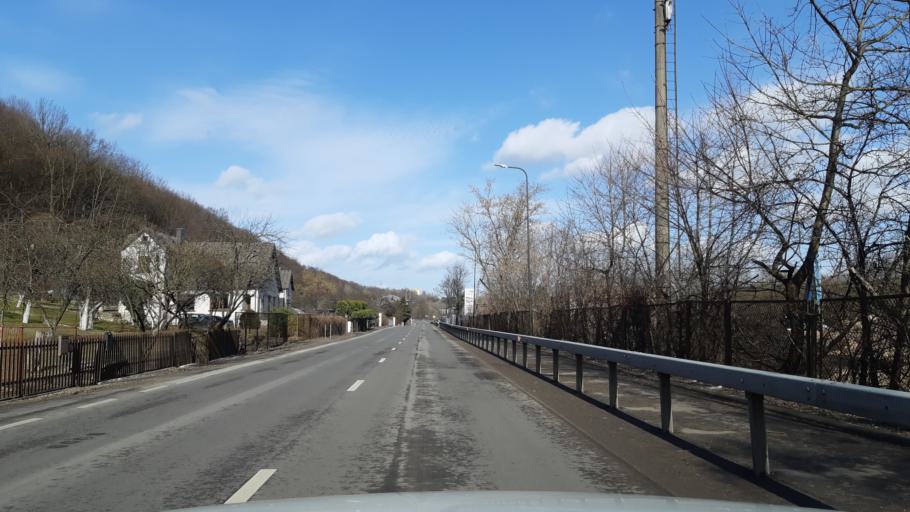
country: LT
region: Kauno apskritis
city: Dainava (Kaunas)
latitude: 54.8779
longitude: 23.9576
